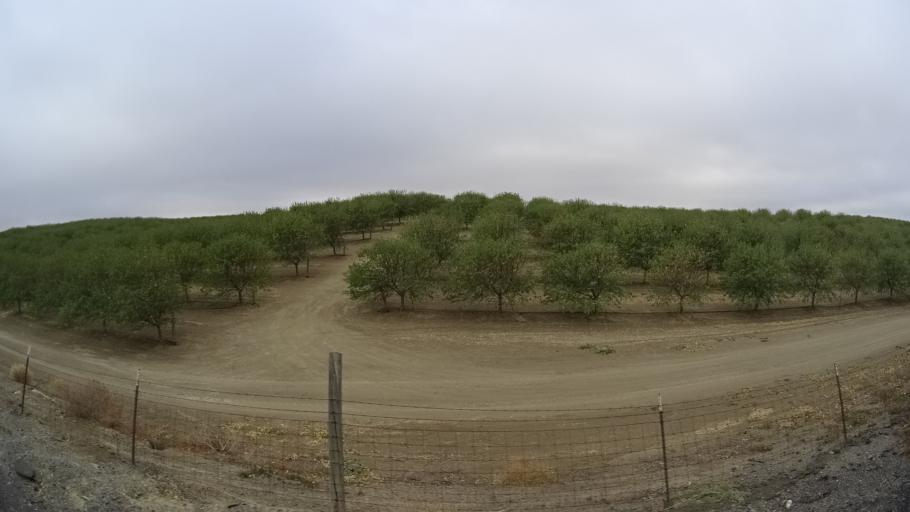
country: US
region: California
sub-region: Yolo County
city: Dunnigan
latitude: 38.8832
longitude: -122.0259
